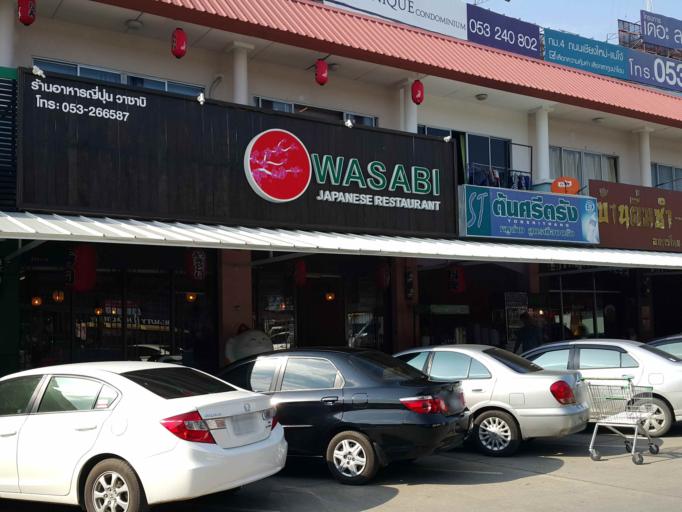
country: TH
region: Chiang Mai
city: San Sai
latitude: 18.8240
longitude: 99.0110
